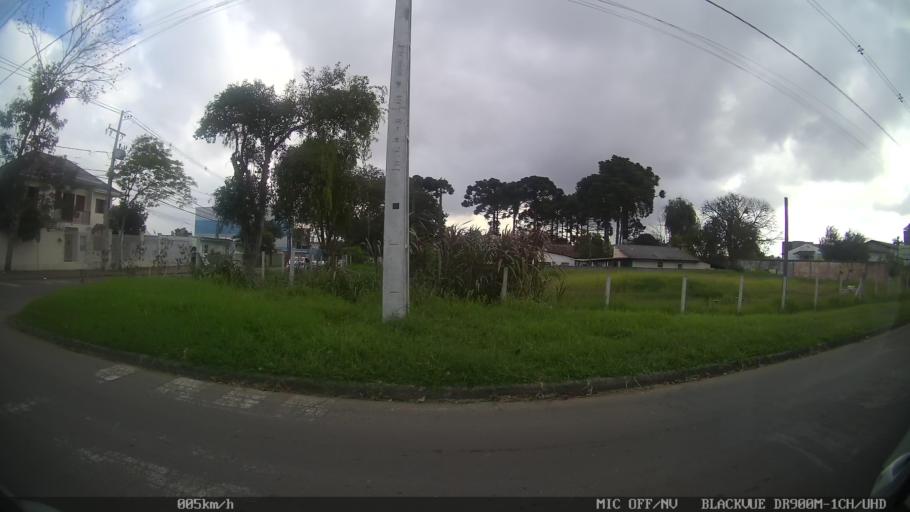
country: BR
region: Parana
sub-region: Pinhais
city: Pinhais
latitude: -25.4357
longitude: -49.1923
